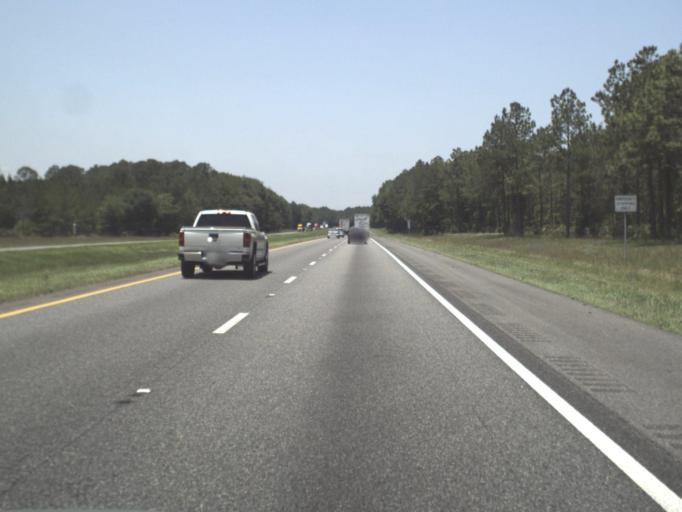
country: US
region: Florida
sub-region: Baker County
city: Macclenny
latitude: 30.2470
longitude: -82.3173
